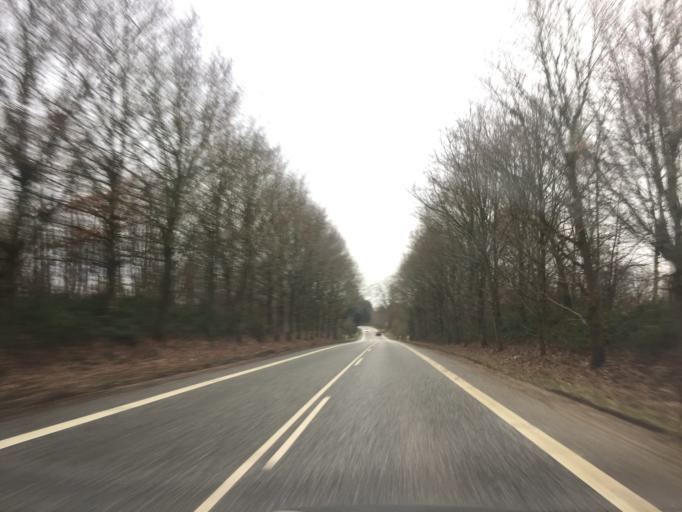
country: DK
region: South Denmark
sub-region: Svendborg Kommune
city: Svendborg
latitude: 55.1066
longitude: 10.6405
